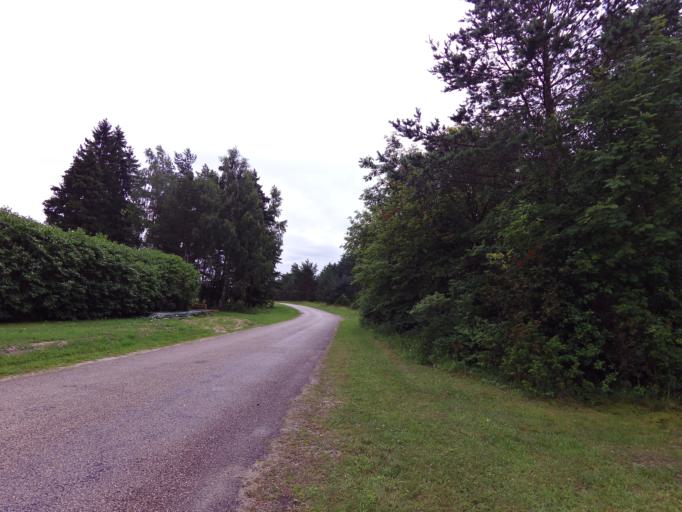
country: EE
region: Laeaene
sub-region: Vormsi vald
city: Hullo
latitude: 59.0125
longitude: 23.3497
